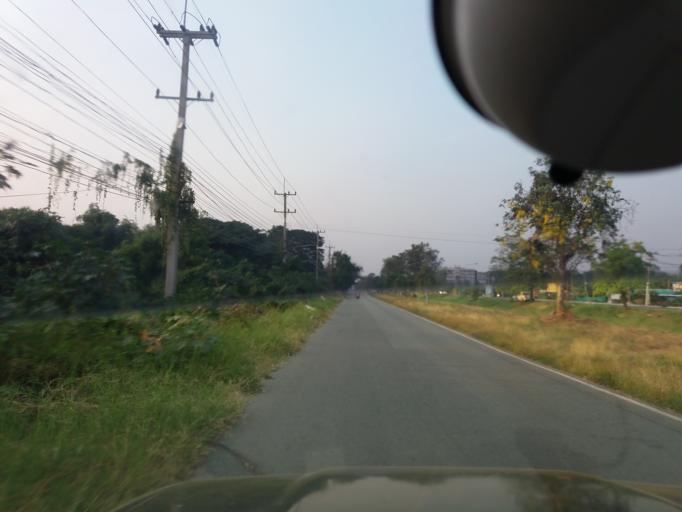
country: TH
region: Sing Buri
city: Sing Buri
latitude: 14.8810
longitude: 100.4026
